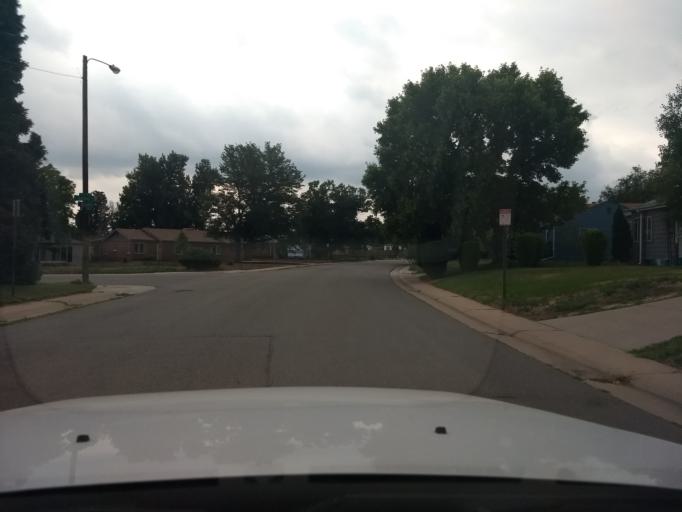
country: US
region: Colorado
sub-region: Denver County
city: Denver
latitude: 39.7067
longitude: -105.0081
